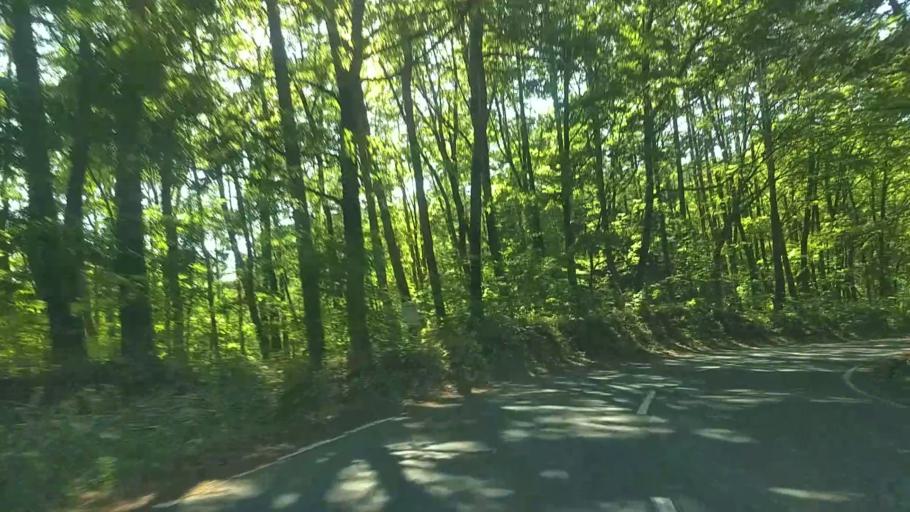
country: JP
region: Yamanashi
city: Nirasaki
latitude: 35.8832
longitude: 138.3771
